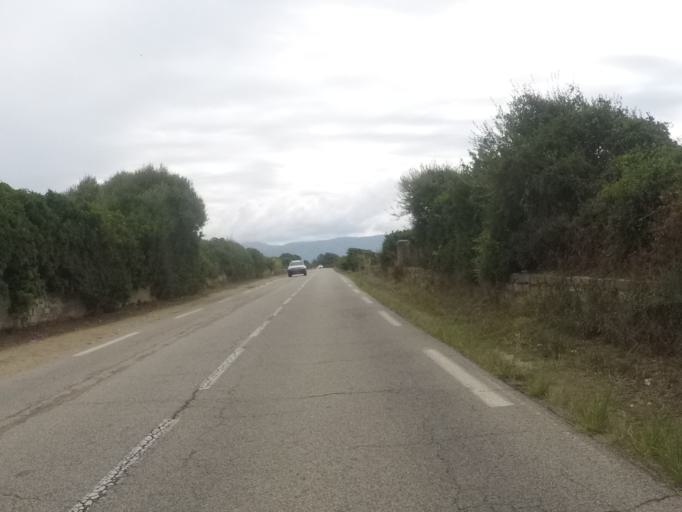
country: FR
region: Corsica
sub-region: Departement de la Corse-du-Sud
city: Propriano
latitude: 41.7076
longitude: 8.8309
